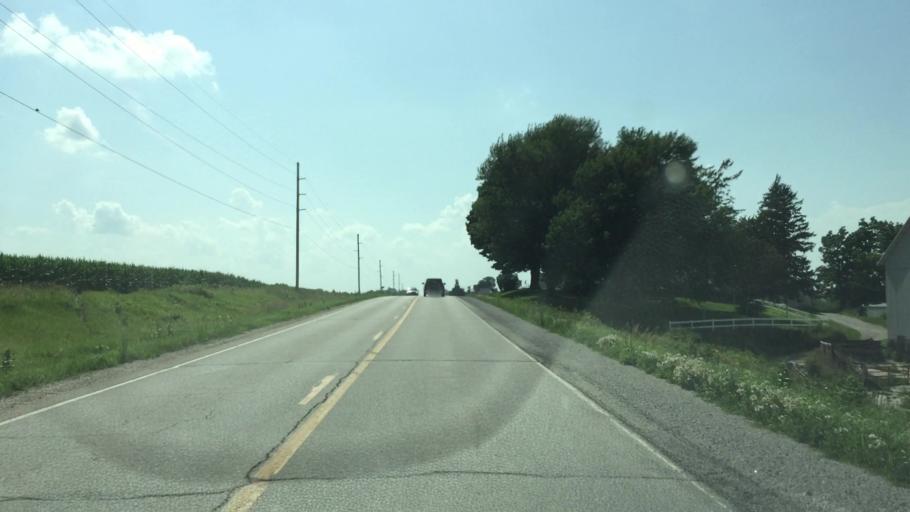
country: US
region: Iowa
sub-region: Linn County
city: Ely
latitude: 41.8474
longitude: -91.5852
